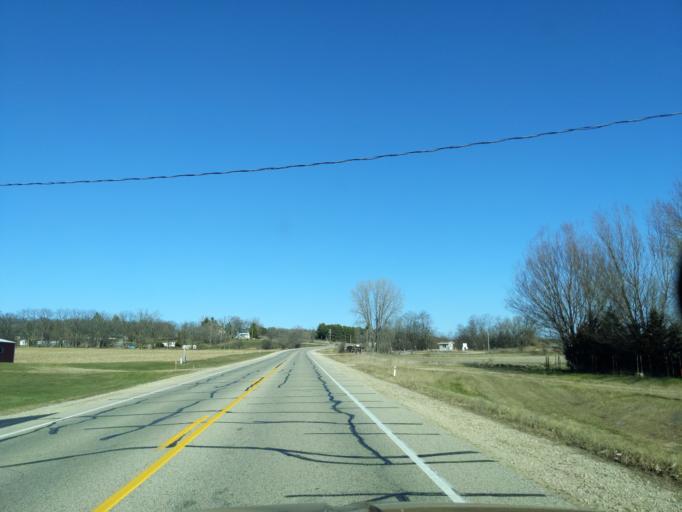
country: US
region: Wisconsin
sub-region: Waushara County
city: Wautoma
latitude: 44.1017
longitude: -89.2891
